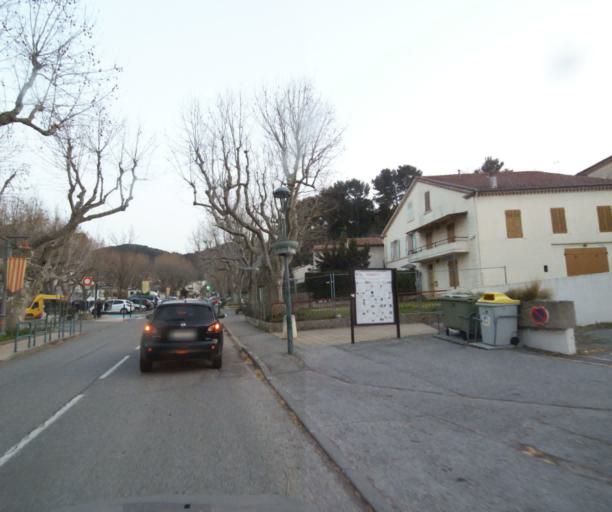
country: FR
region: Provence-Alpes-Cote d'Azur
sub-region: Departement des Bouches-du-Rhone
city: Simiane-Collongue
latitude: 43.4303
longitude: 5.4352
